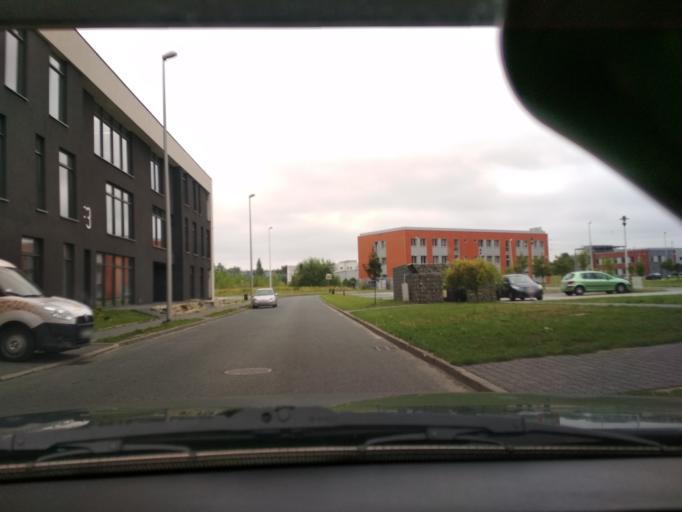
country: PL
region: Silesian Voivodeship
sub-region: Gliwice
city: Gliwice
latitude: 50.2778
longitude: 18.6849
